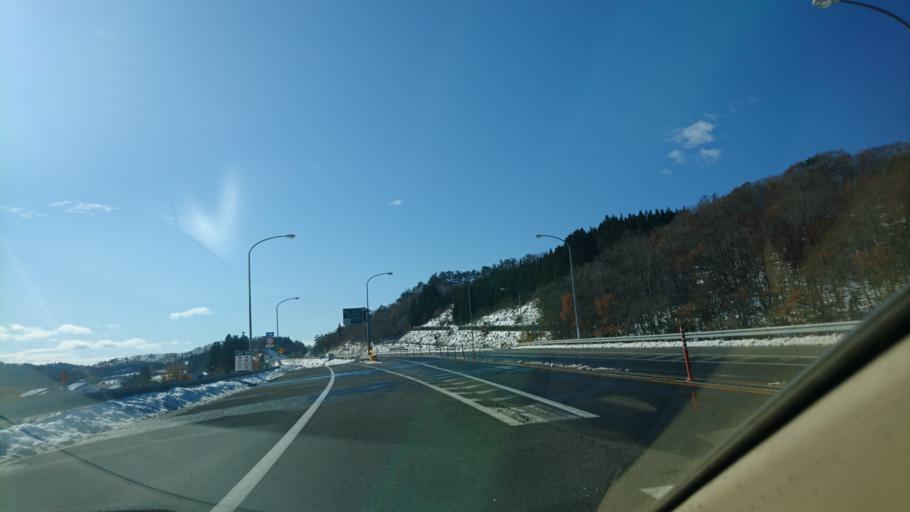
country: JP
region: Akita
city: Yokotemachi
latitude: 39.3146
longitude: 140.7491
